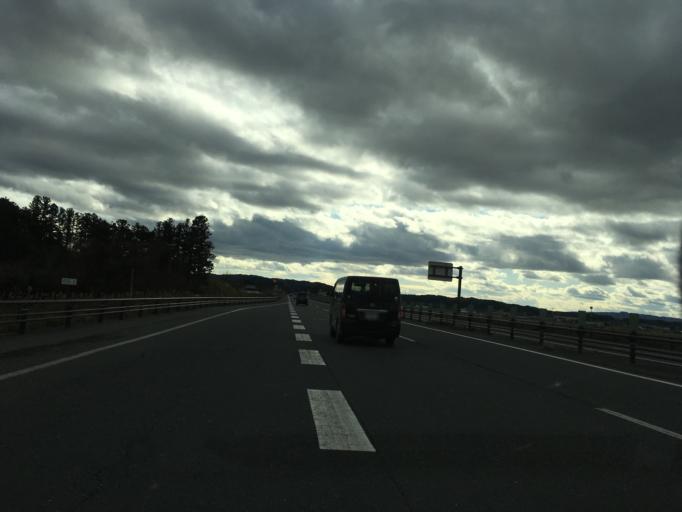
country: JP
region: Miyagi
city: Wakuya
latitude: 38.6730
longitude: 141.2658
